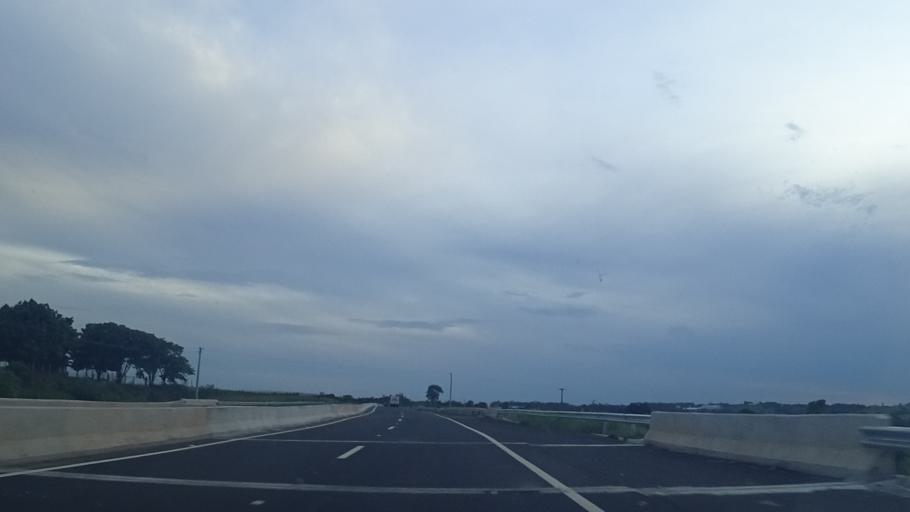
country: BR
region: Sao Paulo
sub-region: Presidente Prudente
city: Presidente Prudente
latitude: -22.1798
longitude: -51.4170
